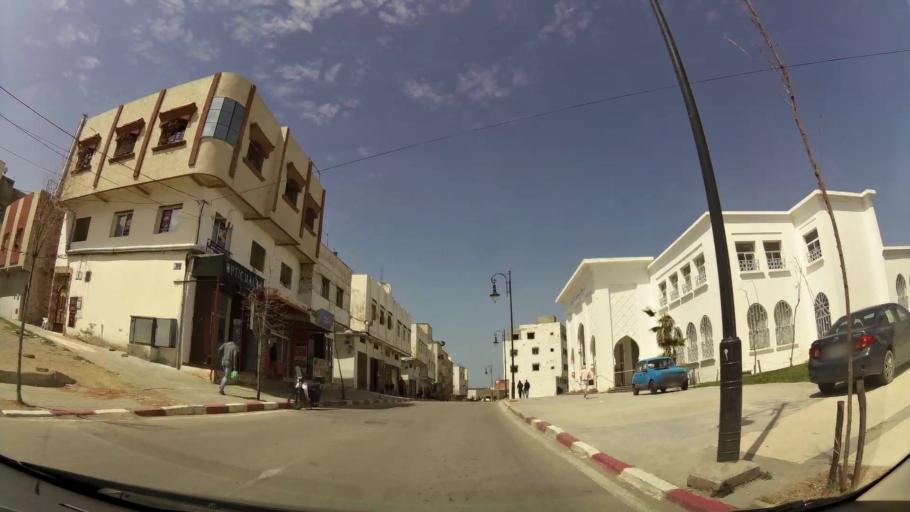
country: MA
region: Tanger-Tetouan
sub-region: Tanger-Assilah
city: Tangier
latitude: 35.7389
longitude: -5.8244
